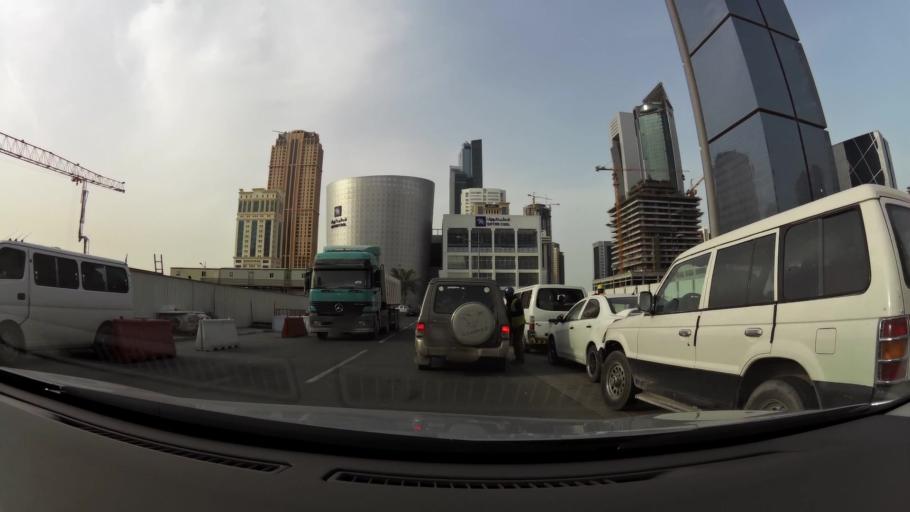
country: QA
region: Baladiyat ad Dawhah
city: Doha
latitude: 25.3212
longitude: 51.5240
